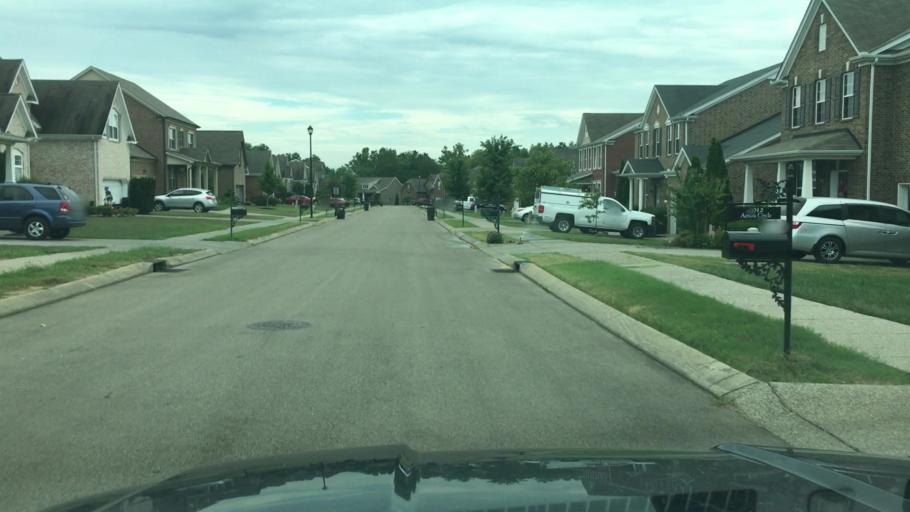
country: US
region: Tennessee
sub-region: Maury County
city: Spring Hill
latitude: 35.7595
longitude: -86.8749
